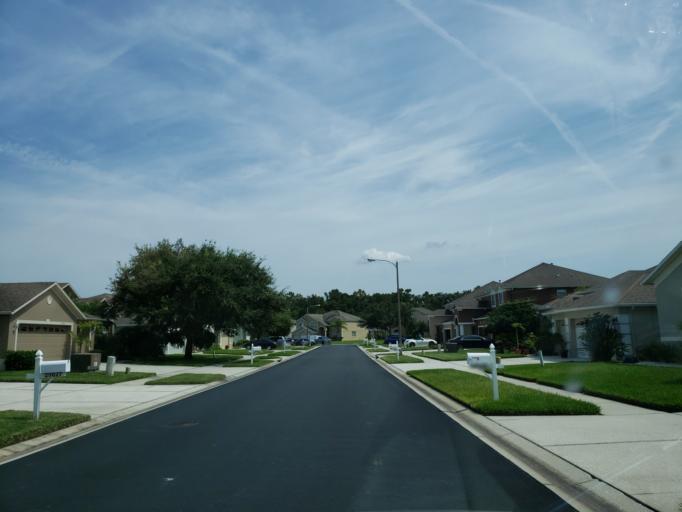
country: US
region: Florida
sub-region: Pasco County
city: Land O' Lakes
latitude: 28.2248
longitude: -82.3922
